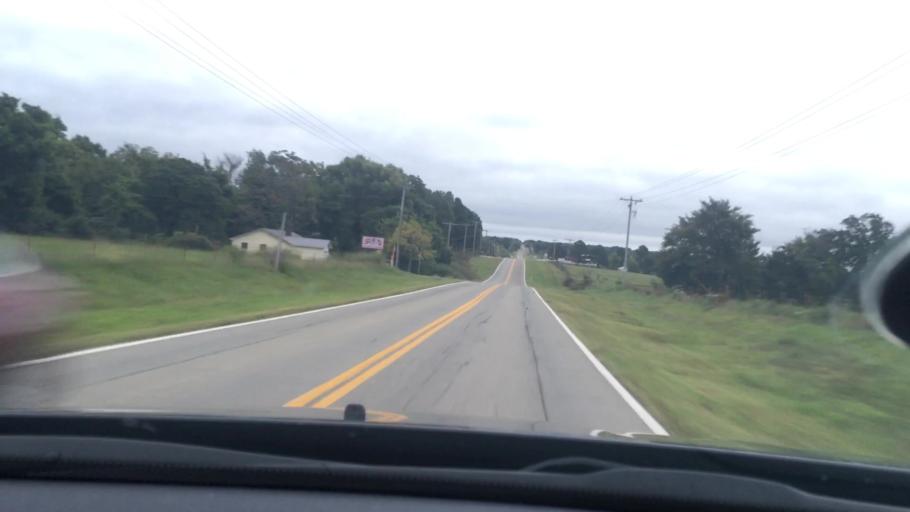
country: US
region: Oklahoma
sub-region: Sequoyah County
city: Vian
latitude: 35.6097
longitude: -94.9864
